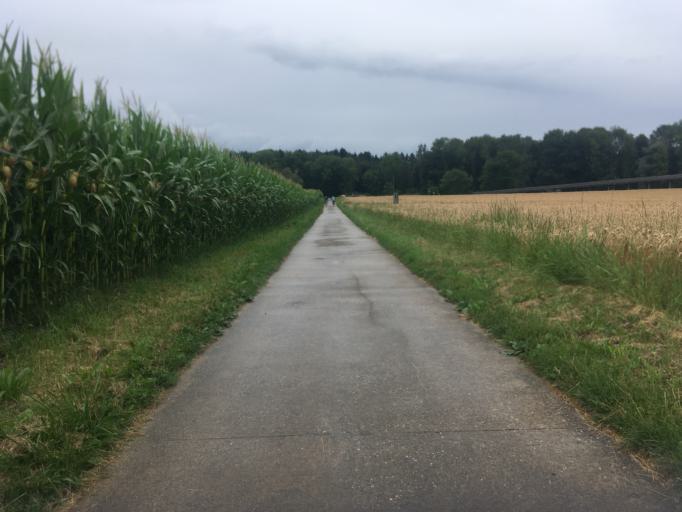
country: CH
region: Fribourg
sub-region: See District
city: Bas-Vully
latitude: 46.9739
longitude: 7.0907
